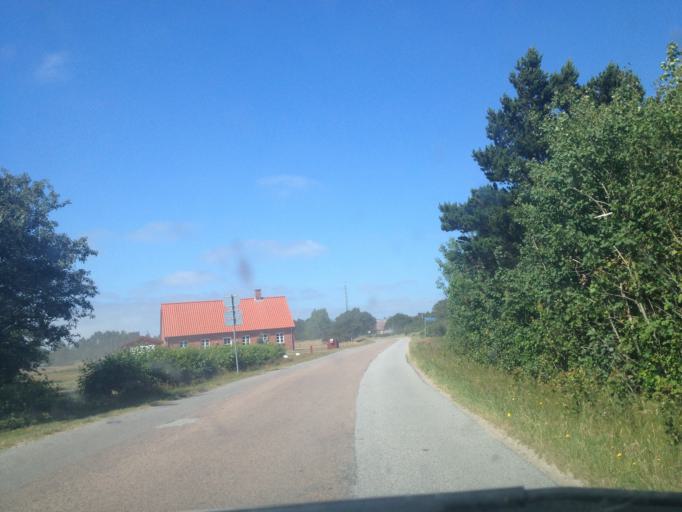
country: DE
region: Schleswig-Holstein
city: List
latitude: 55.0890
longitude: 8.5424
